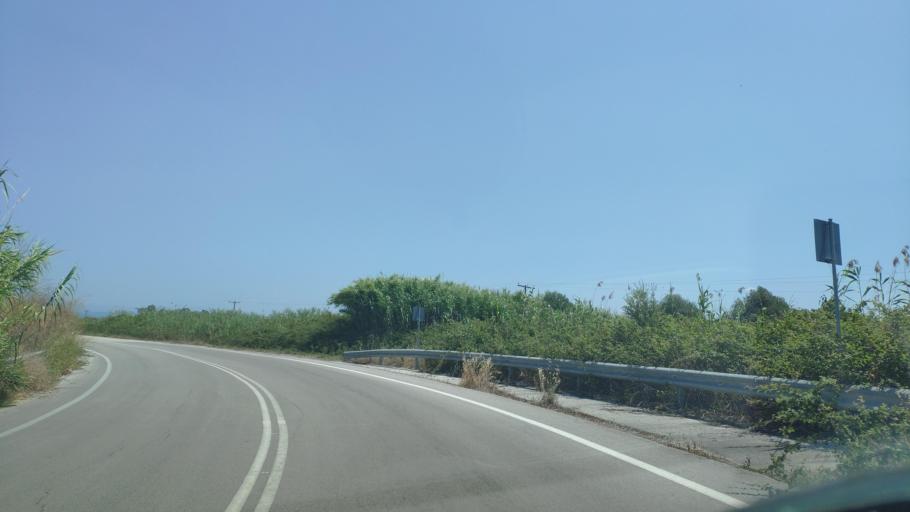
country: GR
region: Epirus
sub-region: Nomos Artas
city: Aneza
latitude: 39.0610
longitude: 20.8720
